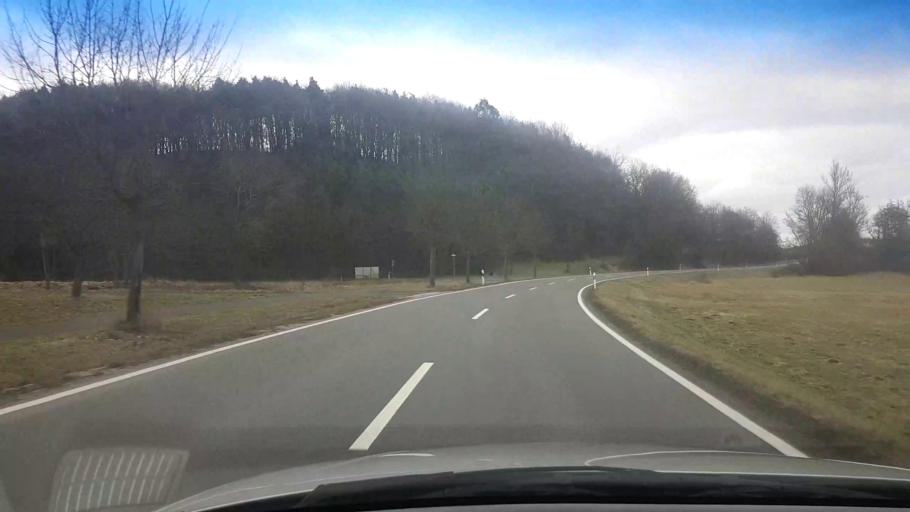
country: DE
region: Bavaria
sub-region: Regierungsbezirk Unterfranken
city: Eltmann
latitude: 49.9226
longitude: 10.6725
